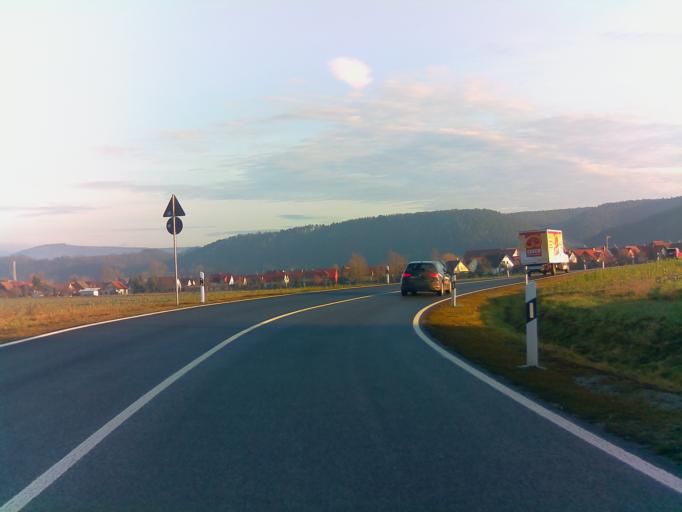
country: DE
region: Thuringia
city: Schops
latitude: 50.8402
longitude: 11.6010
